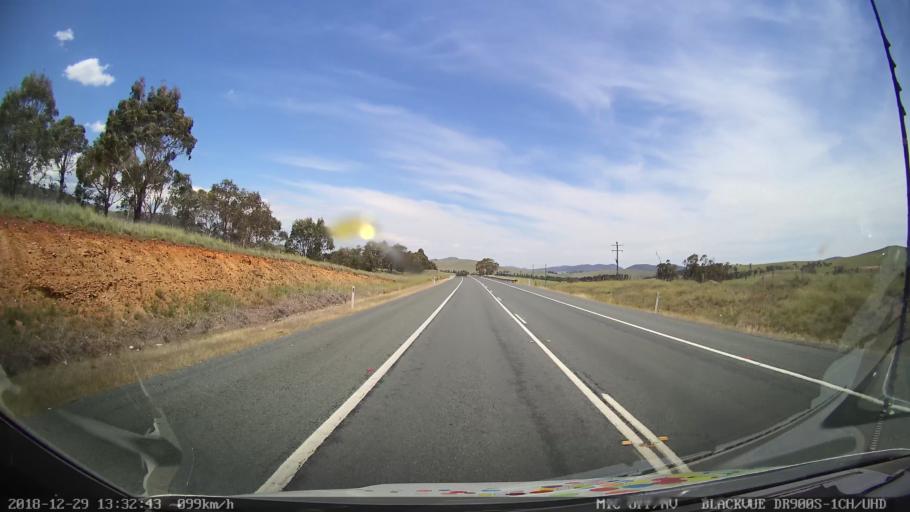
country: AU
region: New South Wales
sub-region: Cooma-Monaro
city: Cooma
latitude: -35.9346
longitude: 149.1484
